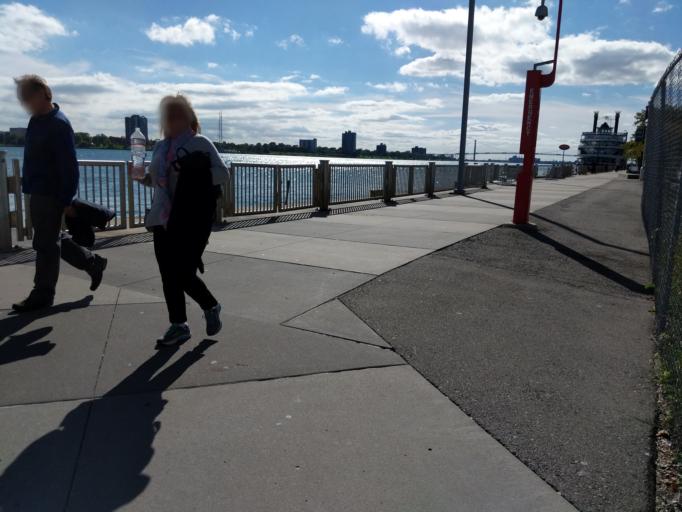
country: US
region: Michigan
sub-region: Wayne County
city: Detroit
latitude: 42.3270
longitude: -83.0421
